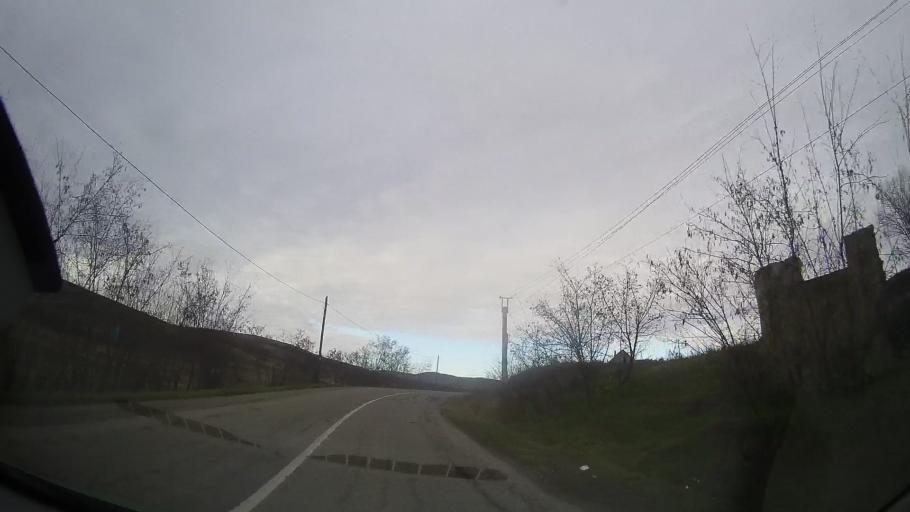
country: RO
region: Cluj
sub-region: Comuna Camarasu
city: Camarasu
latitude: 46.8073
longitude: 24.1447
